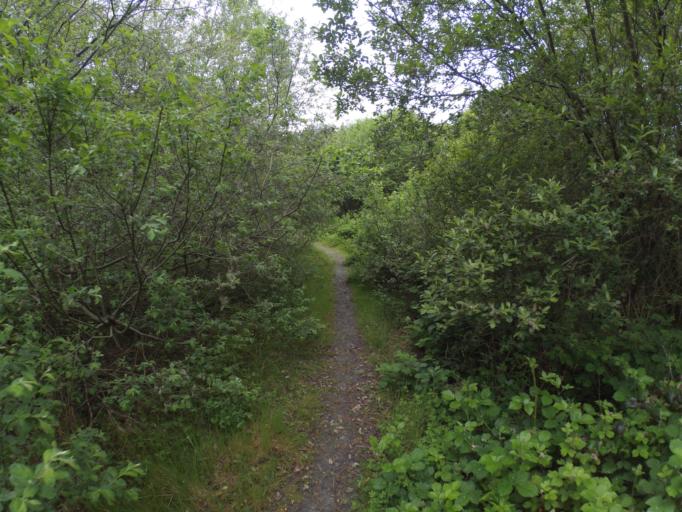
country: GB
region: Wales
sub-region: County of Ceredigion
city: Llangybi
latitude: 52.1688
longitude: -4.0612
